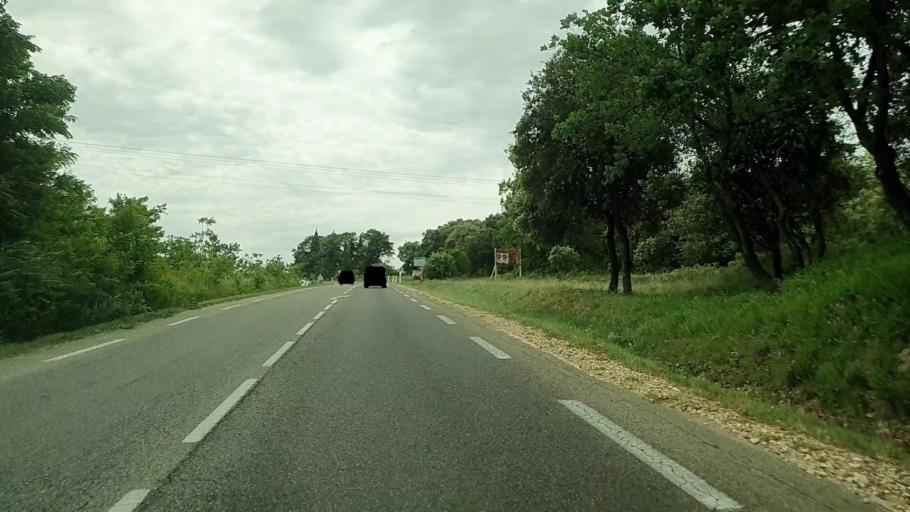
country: FR
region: Languedoc-Roussillon
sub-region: Departement du Gard
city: Connaux
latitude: 44.0600
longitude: 4.5710
